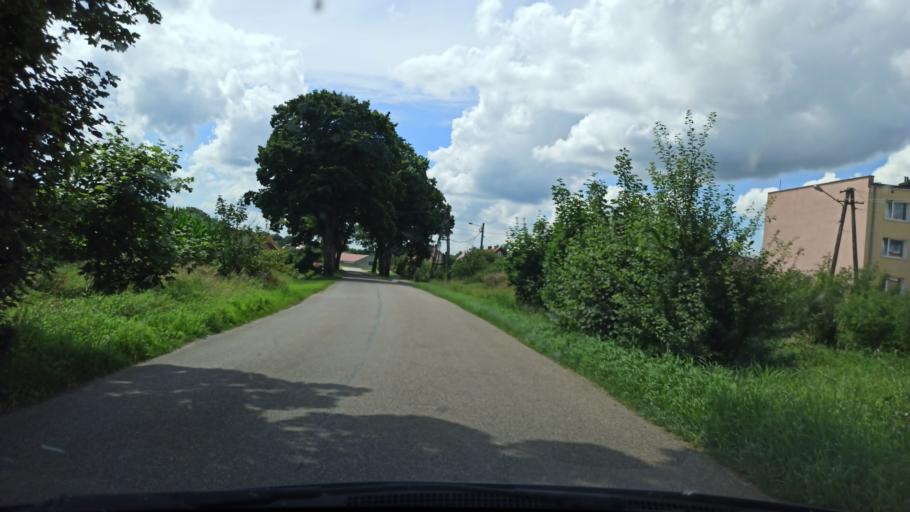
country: PL
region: Warmian-Masurian Voivodeship
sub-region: Powiat ostrodzki
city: Morag
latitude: 53.8574
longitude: 19.9858
